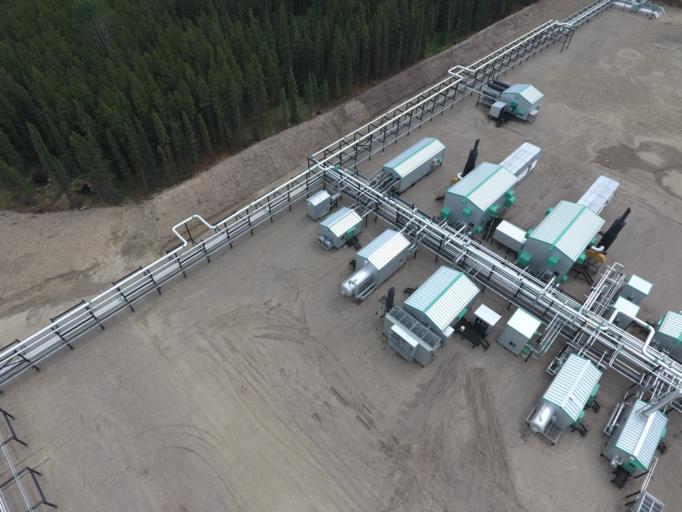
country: CA
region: Alberta
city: Edson
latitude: 52.8420
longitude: -116.0406
